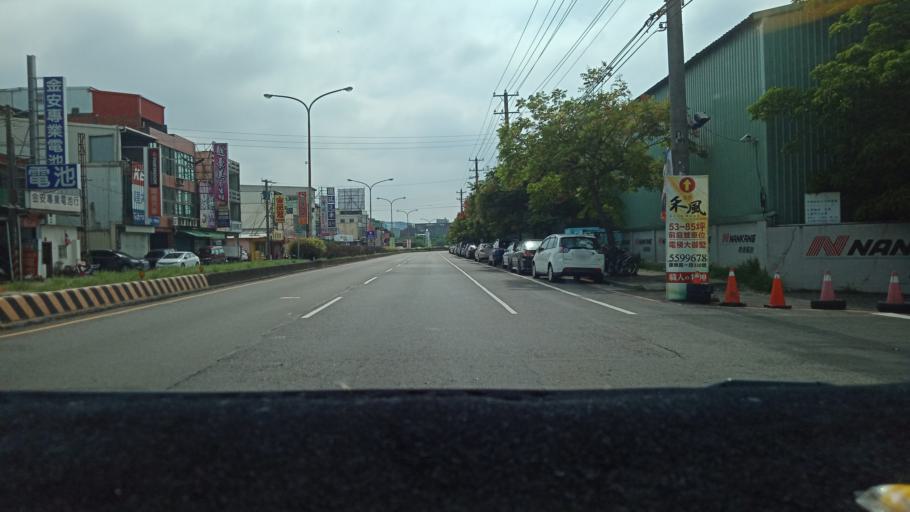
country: TW
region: Taiwan
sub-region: Hsinchu
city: Zhubei
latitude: 24.8780
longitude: 121.0056
